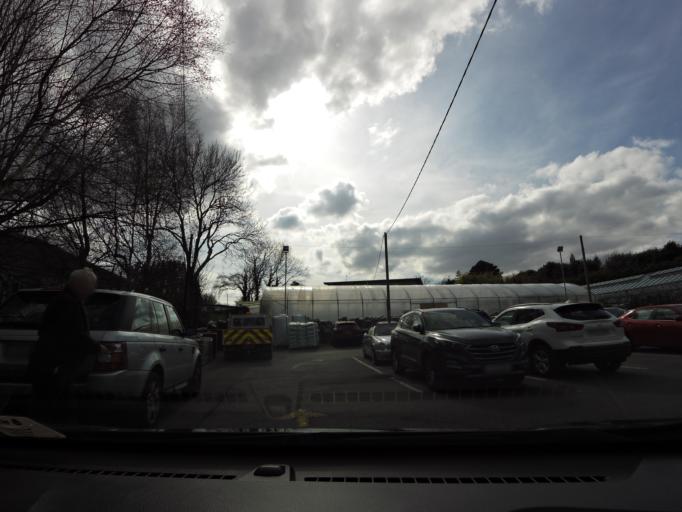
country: IE
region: Connaught
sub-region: County Galway
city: Gaillimh
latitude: 53.2921
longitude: -9.0739
